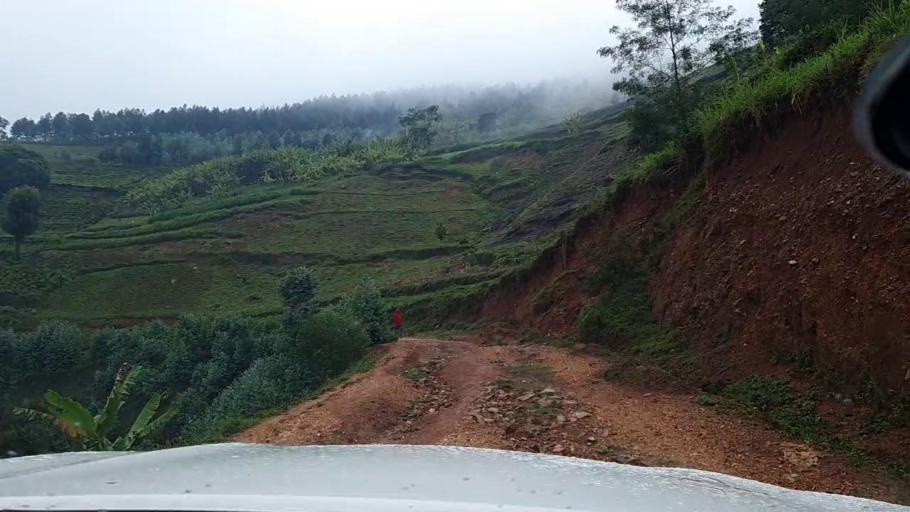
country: RW
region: Western Province
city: Kibuye
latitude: -2.1387
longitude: 29.4581
